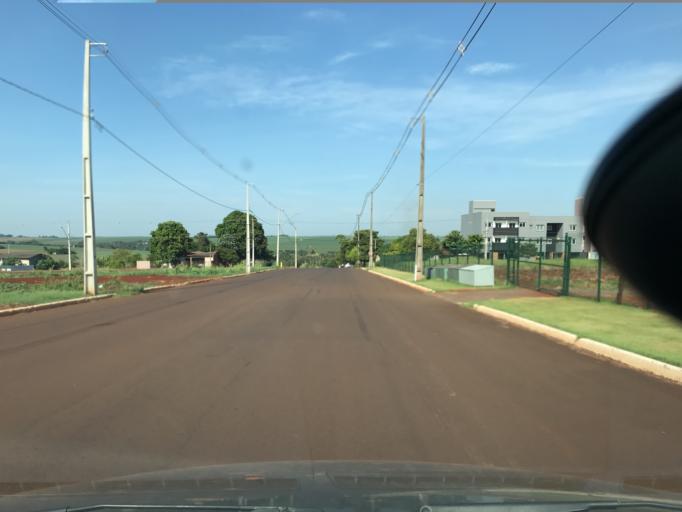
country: BR
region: Parana
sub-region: Palotina
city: Palotina
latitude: -24.2977
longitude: -53.8415
